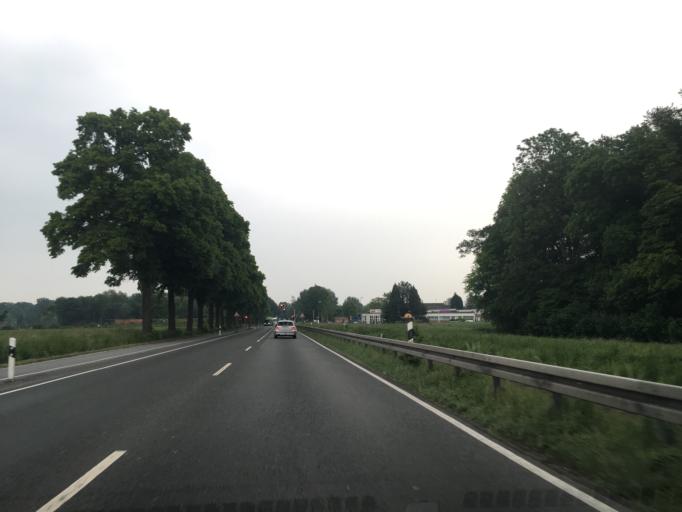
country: DE
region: North Rhine-Westphalia
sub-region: Regierungsbezirk Munster
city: Muenster
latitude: 51.9731
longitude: 7.6908
